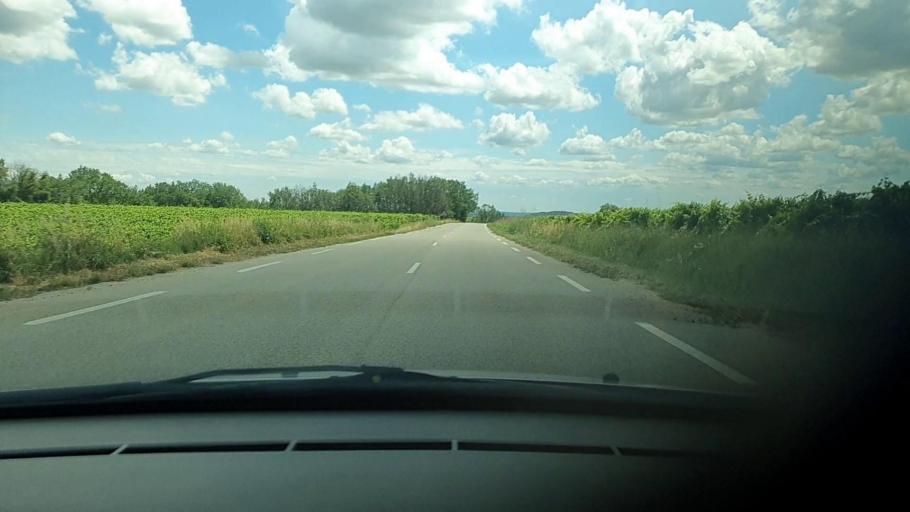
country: FR
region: Languedoc-Roussillon
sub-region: Departement du Gard
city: Moussac
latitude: 44.0464
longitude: 4.2317
